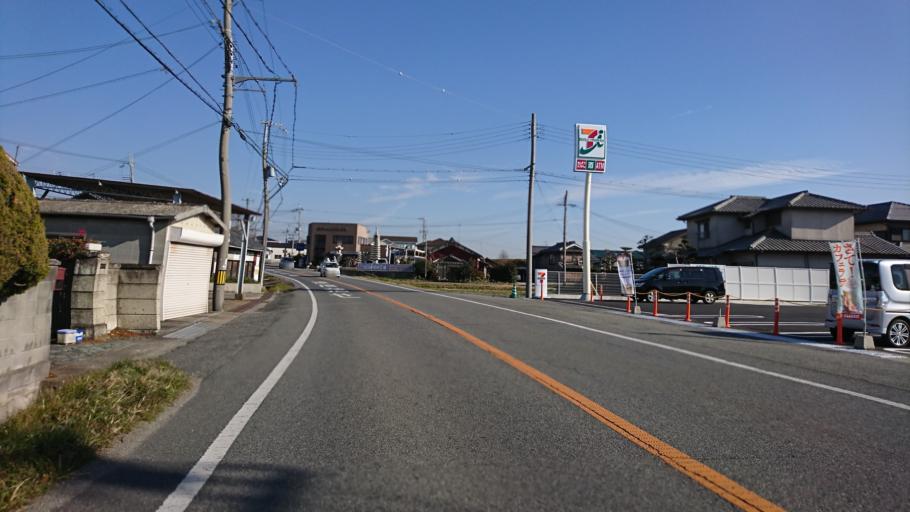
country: JP
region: Hyogo
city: Ono
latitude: 34.7982
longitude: 134.8952
